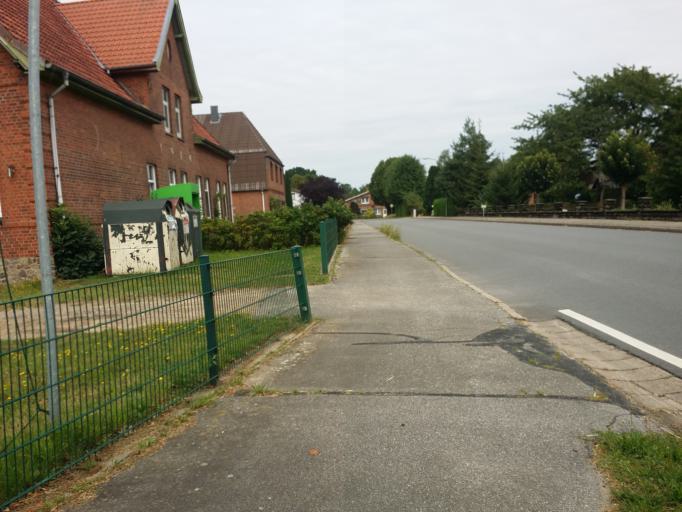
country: DE
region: Schleswig-Holstein
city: Huje
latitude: 53.9751
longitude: 9.4372
